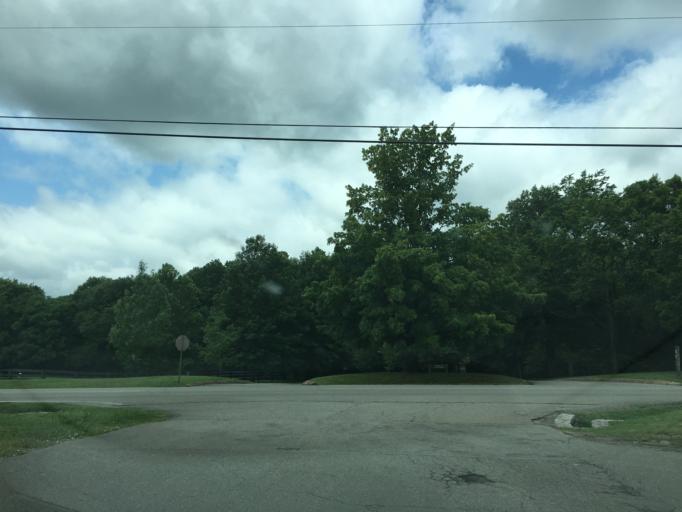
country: US
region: Tennessee
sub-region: Davidson County
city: Forest Hills
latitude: 36.0524
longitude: -86.8998
